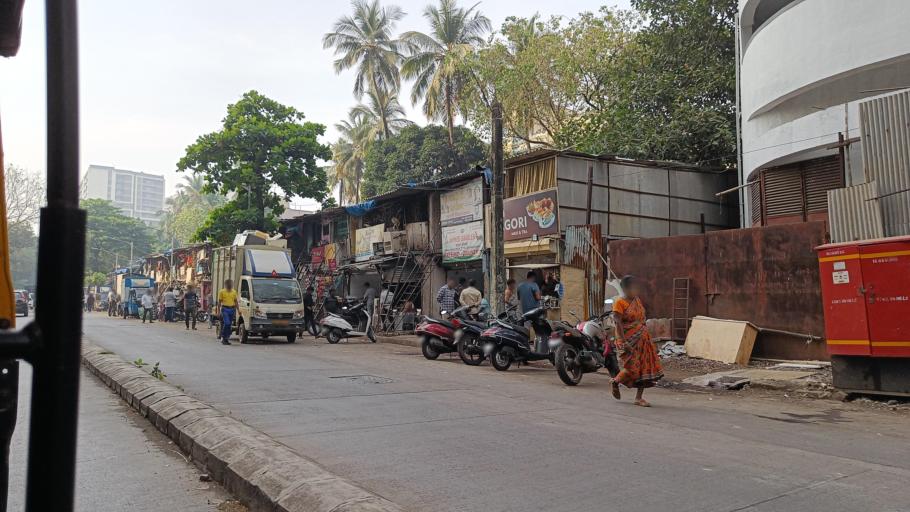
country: IN
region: Maharashtra
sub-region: Mumbai Suburban
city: Mumbai
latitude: 19.1261
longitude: 72.8289
